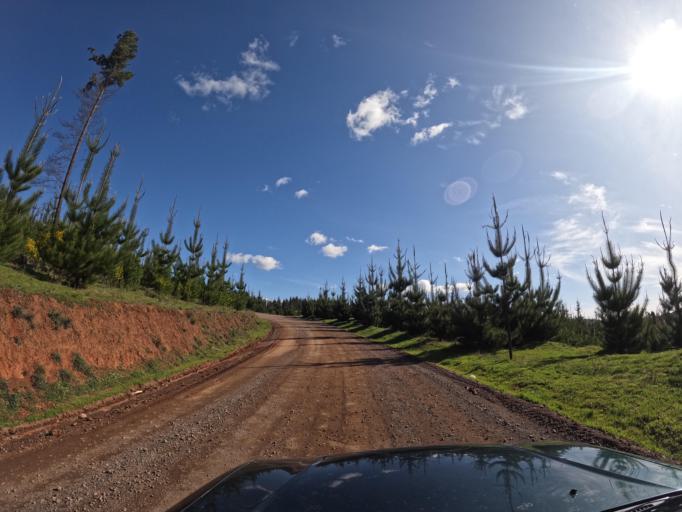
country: CL
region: Biobio
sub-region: Provincia de Biobio
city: La Laja
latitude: -37.0894
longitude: -72.8289
